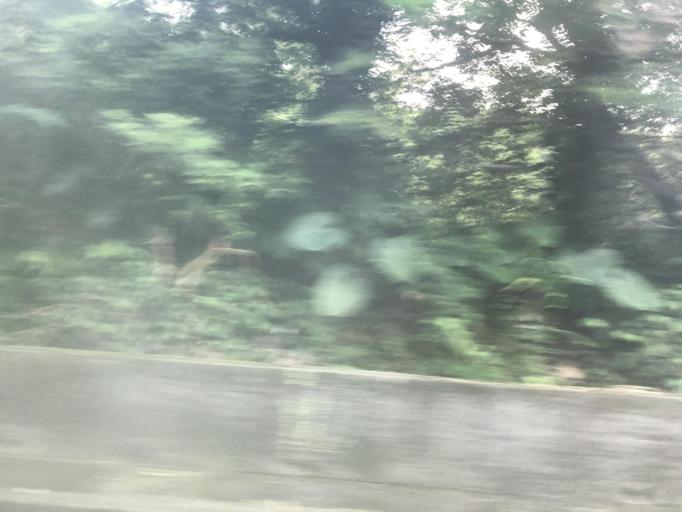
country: TW
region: Taiwan
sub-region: Keelung
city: Keelung
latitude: 25.1714
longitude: 121.6581
